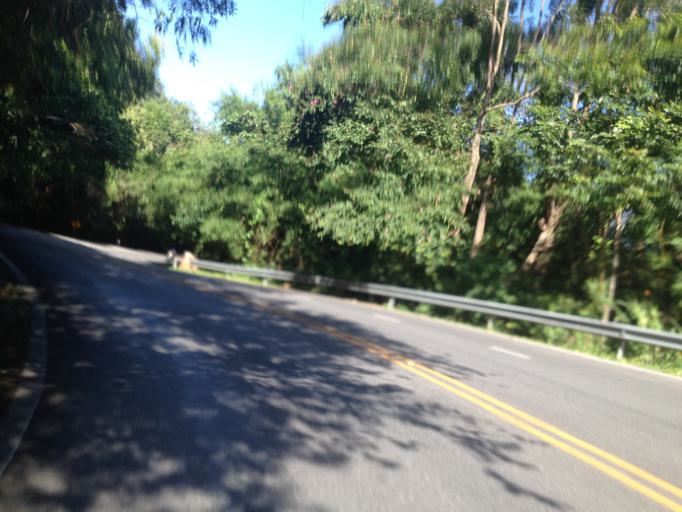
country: TH
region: Chiang Mai
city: Chiang Mai
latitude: 18.7923
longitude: 98.9252
